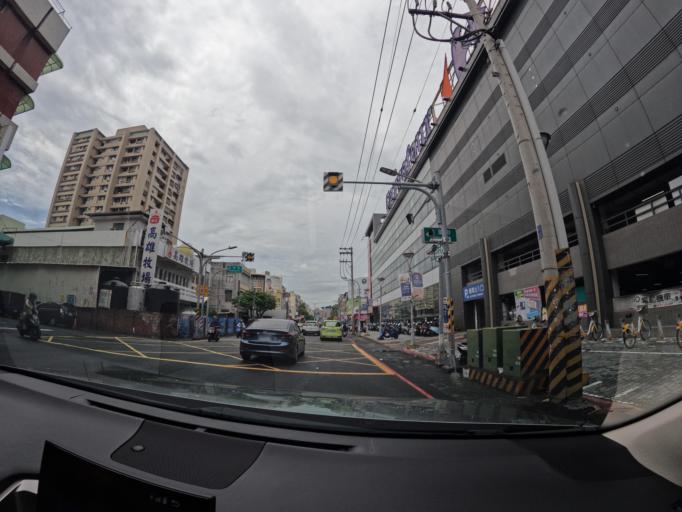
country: TW
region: Kaohsiung
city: Kaohsiung
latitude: 22.6529
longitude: 120.3184
